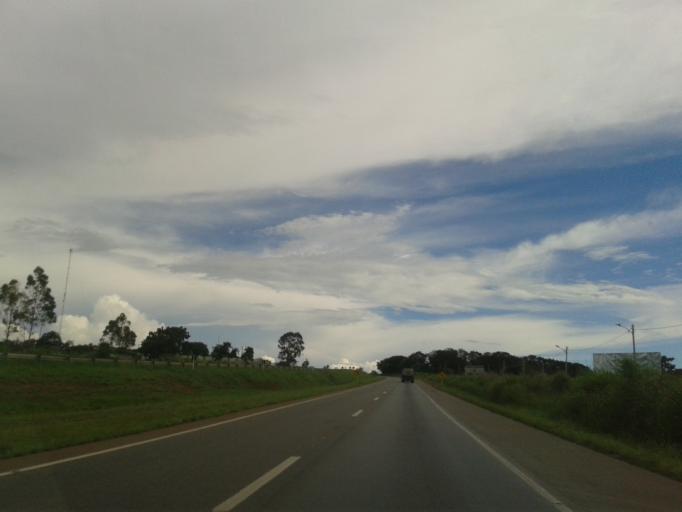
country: BR
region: Goias
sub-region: Aparecida De Goiania
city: Aparecida de Goiania
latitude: -16.8906
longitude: -49.2552
